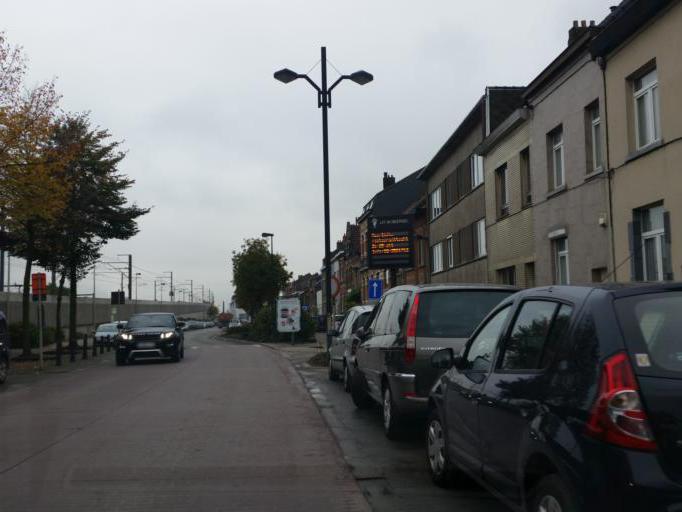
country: BE
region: Flanders
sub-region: Provincie Vlaams-Brabant
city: Beersel
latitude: 50.7663
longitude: 4.2742
